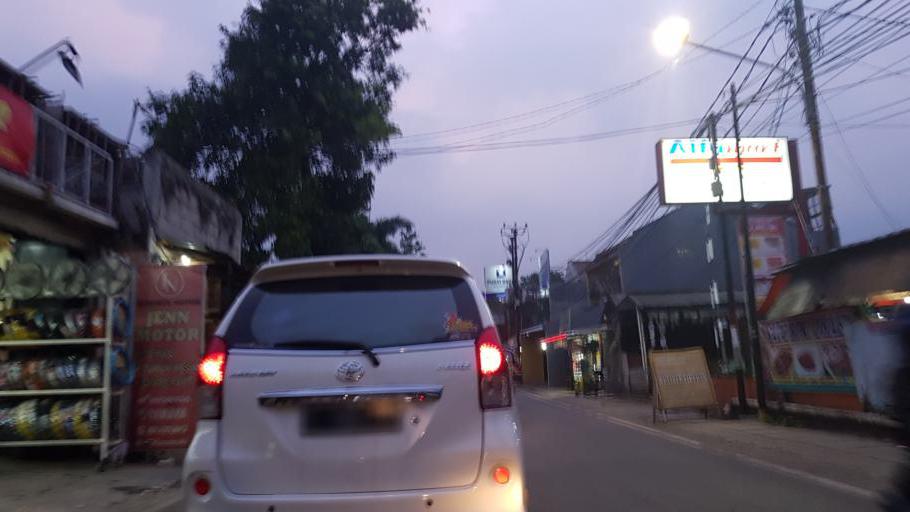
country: ID
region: West Java
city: Depok
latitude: -6.3636
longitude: 106.8070
